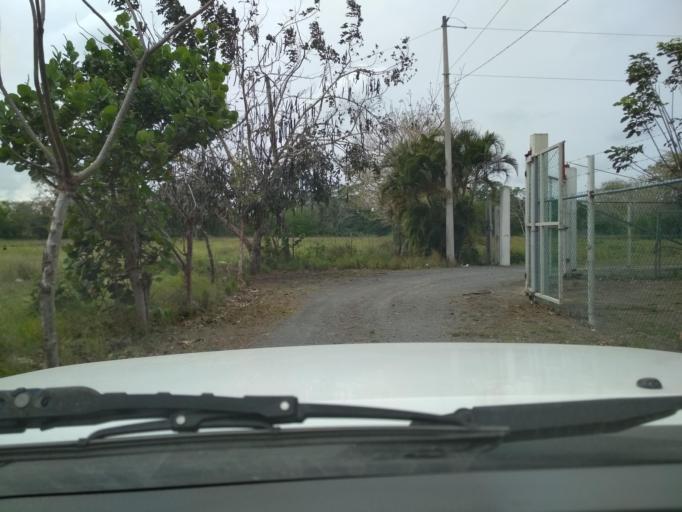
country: MX
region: Veracruz
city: El Tejar
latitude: 19.0683
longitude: -96.1369
